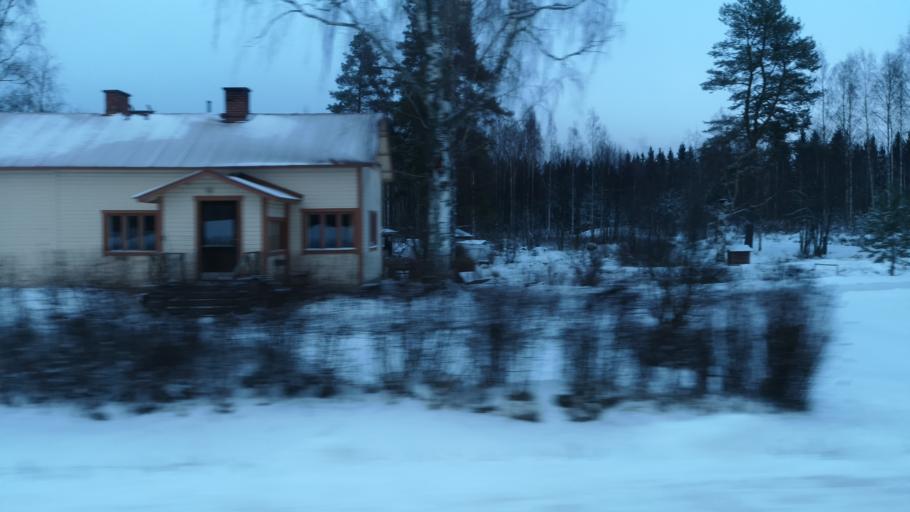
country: FI
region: Southern Savonia
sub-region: Savonlinna
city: Enonkoski
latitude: 62.1071
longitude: 28.6299
